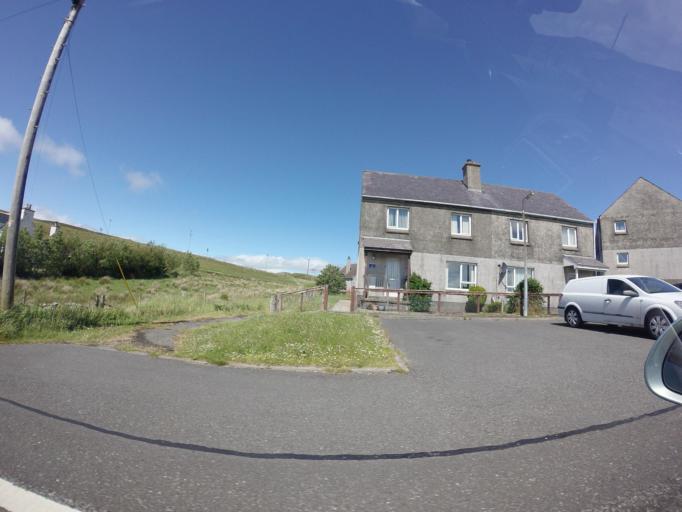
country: GB
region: Scotland
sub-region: Eilean Siar
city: Stornoway
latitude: 58.0915
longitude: -6.6087
